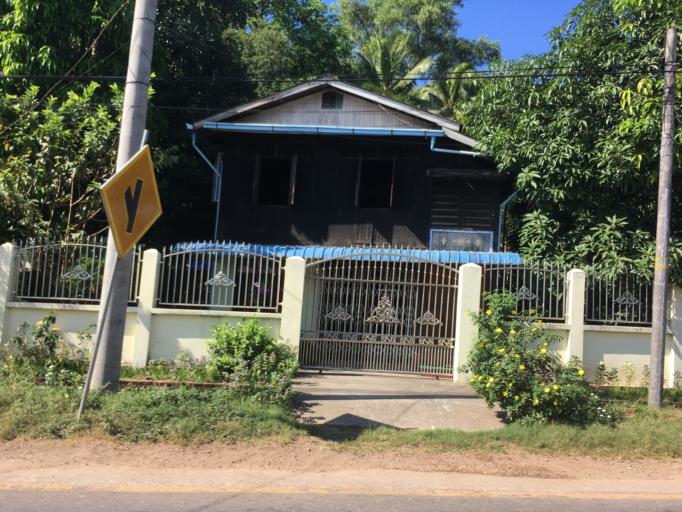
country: MM
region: Mon
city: Mawlamyine
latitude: 16.4860
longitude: 97.6312
